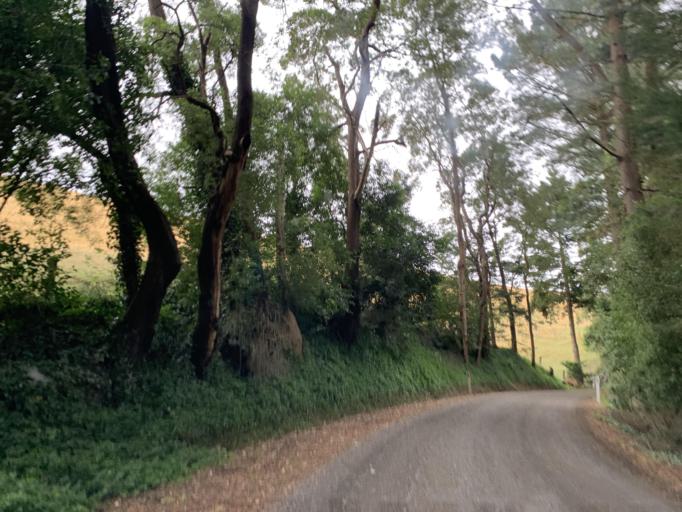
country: AU
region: Victoria
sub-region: Baw Baw
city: Warragul
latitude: -38.3272
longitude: 145.8414
